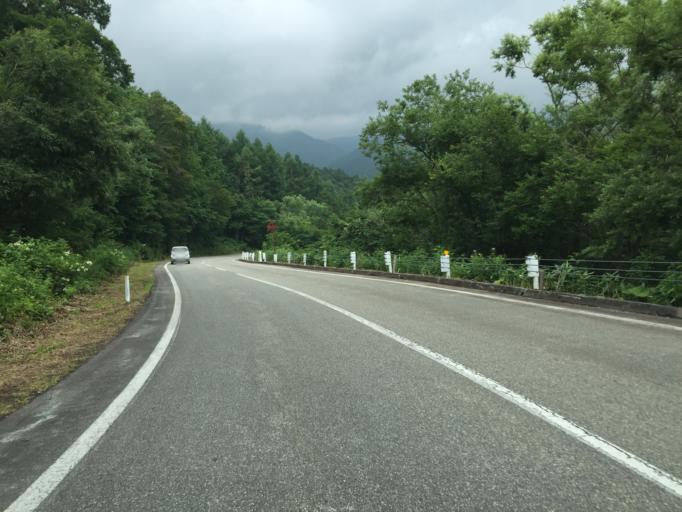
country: JP
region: Fukushima
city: Inawashiro
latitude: 37.6720
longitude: 140.1375
